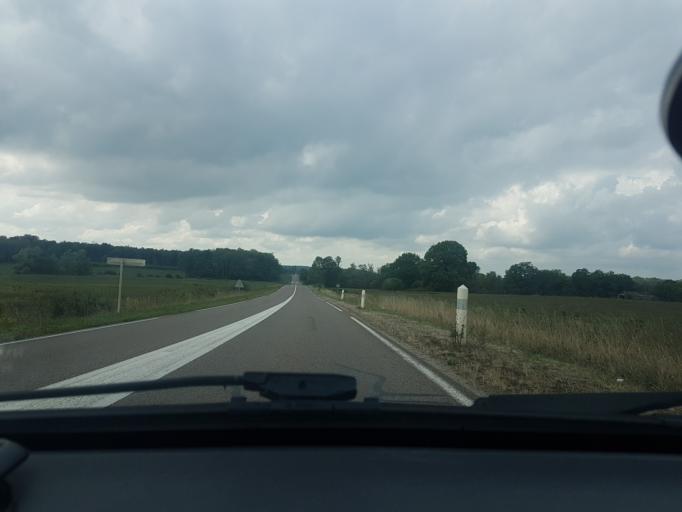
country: FR
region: Franche-Comte
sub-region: Departement de la Haute-Saone
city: Villersexel
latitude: 47.5437
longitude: 6.5063
